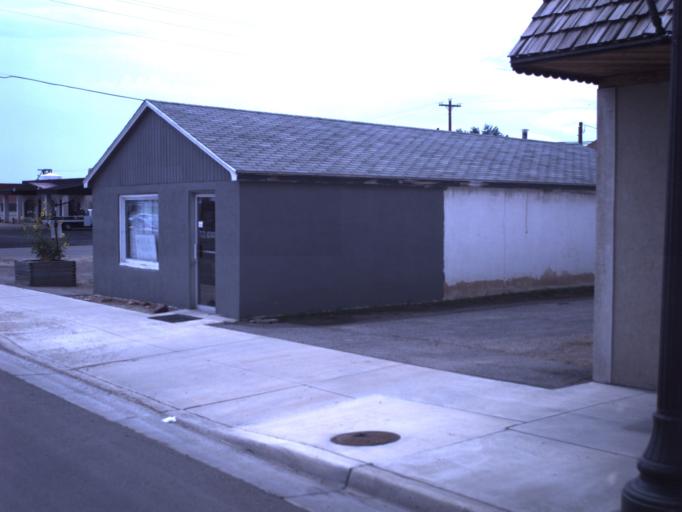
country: US
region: Utah
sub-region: Duchesne County
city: Roosevelt
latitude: 40.2959
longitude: -109.9889
